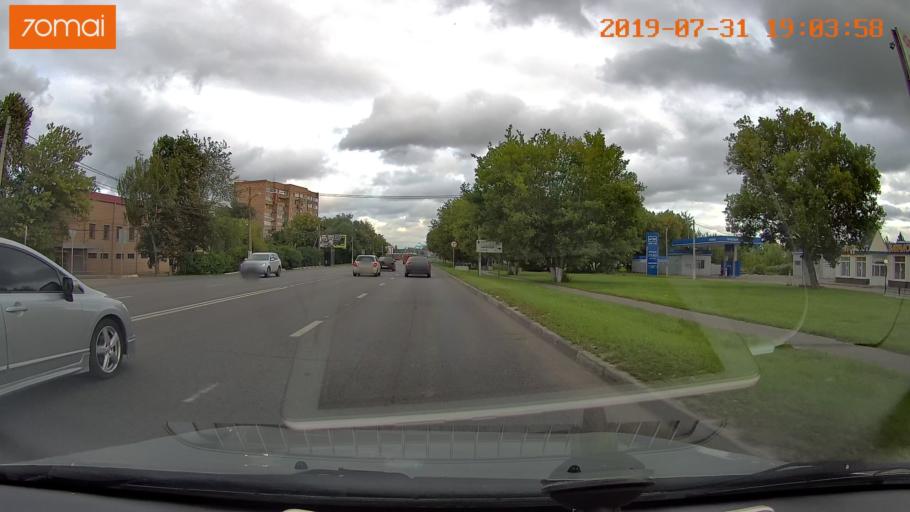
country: RU
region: Moskovskaya
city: Raduzhnyy
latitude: 55.1117
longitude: 38.7388
